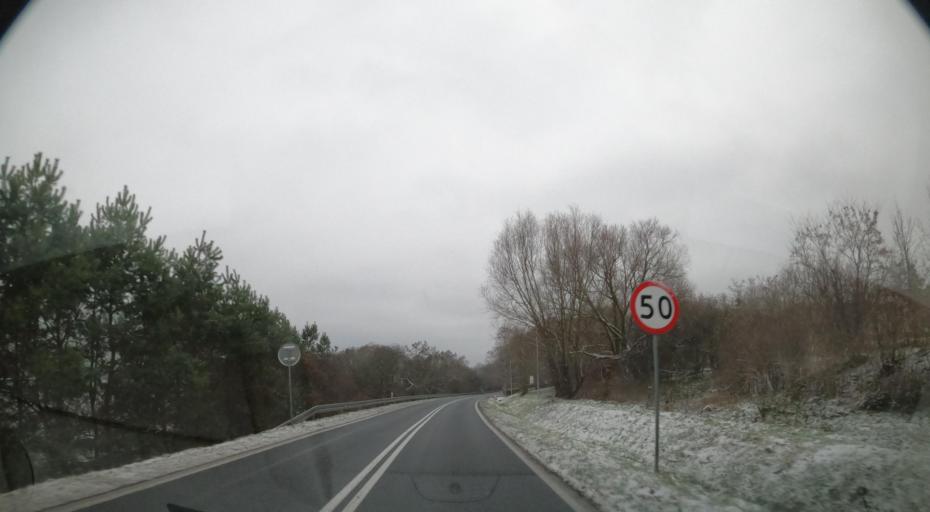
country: PL
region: Masovian Voivodeship
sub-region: Powiat plocki
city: Maszewo Duze
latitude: 52.5704
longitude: 19.5721
